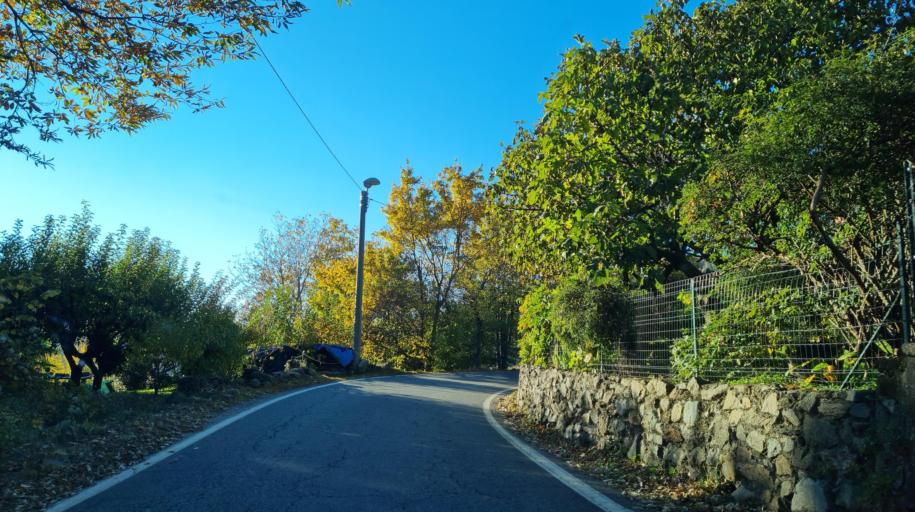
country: IT
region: Piedmont
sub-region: Provincia di Torino
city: Lessolo
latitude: 45.4748
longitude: 7.8115
